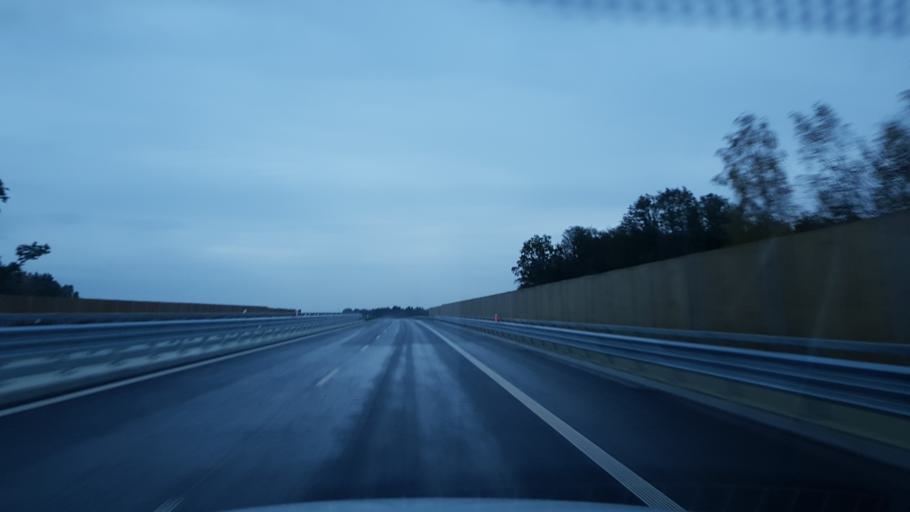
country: PL
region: West Pomeranian Voivodeship
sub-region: Powiat gryficki
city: Brojce
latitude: 53.9571
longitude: 15.4165
